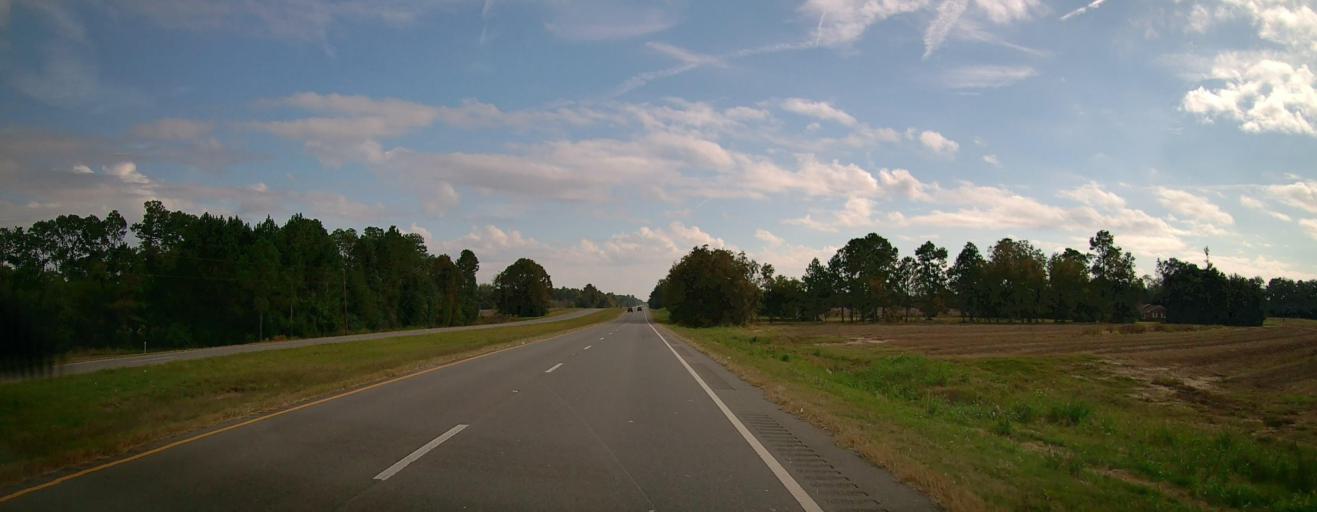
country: US
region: Georgia
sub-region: Thomas County
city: Meigs
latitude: 31.0275
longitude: -84.0610
